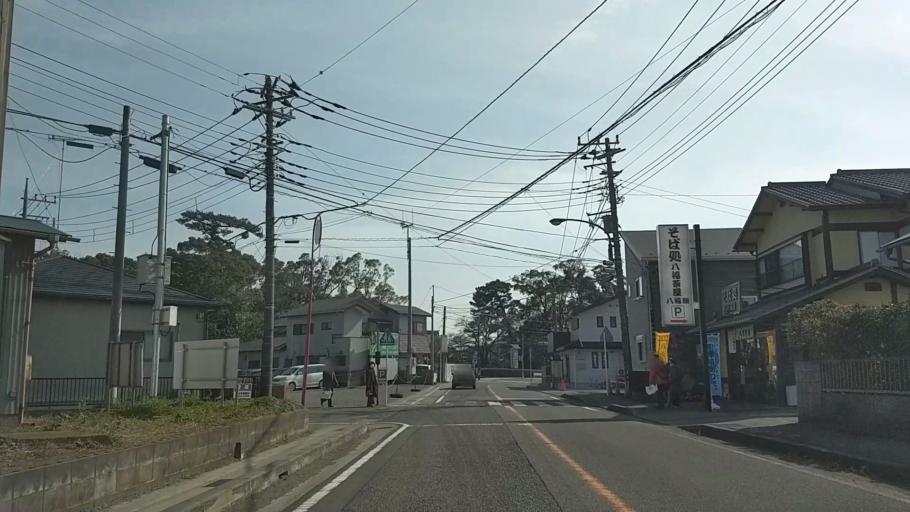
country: JP
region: Kanagawa
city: Chigasaki
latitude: 35.3791
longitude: 139.3806
